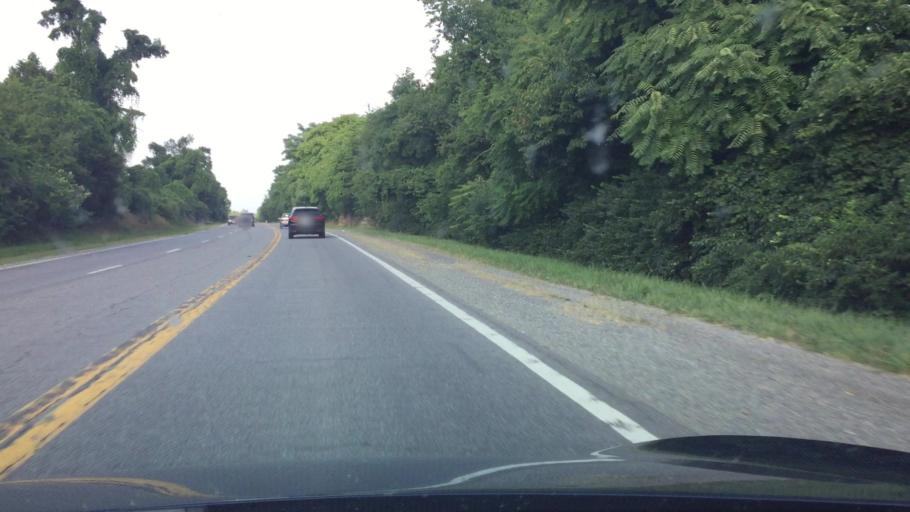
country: US
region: Virginia
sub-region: Pulaski County
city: Dublin
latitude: 37.1291
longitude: -80.6408
